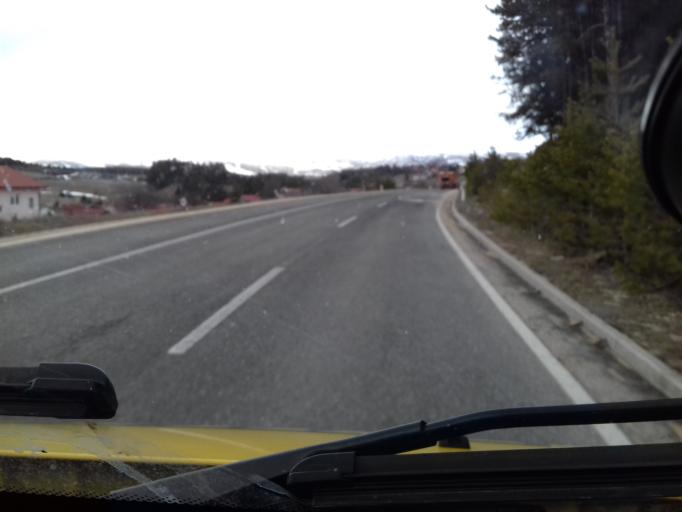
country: BA
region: Federation of Bosnia and Herzegovina
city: Tomislavgrad
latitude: 43.7245
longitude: 17.2259
